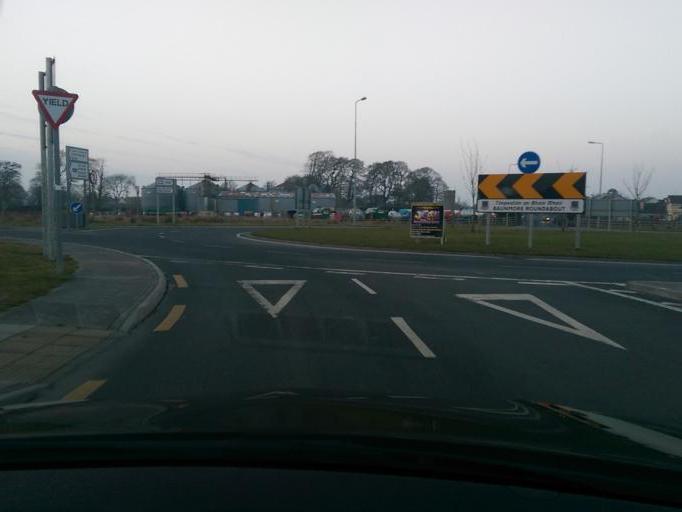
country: IE
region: Connaught
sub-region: County Galway
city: Athenry
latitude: 53.2935
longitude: -8.7434
